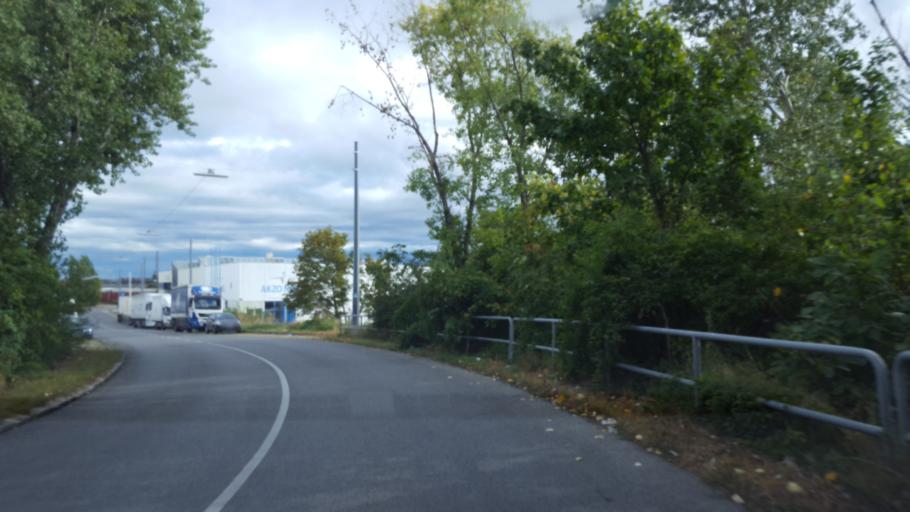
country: AT
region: Lower Austria
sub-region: Politischer Bezirk Wien-Umgebung
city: Schwechat
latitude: 48.1460
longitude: 16.4603
